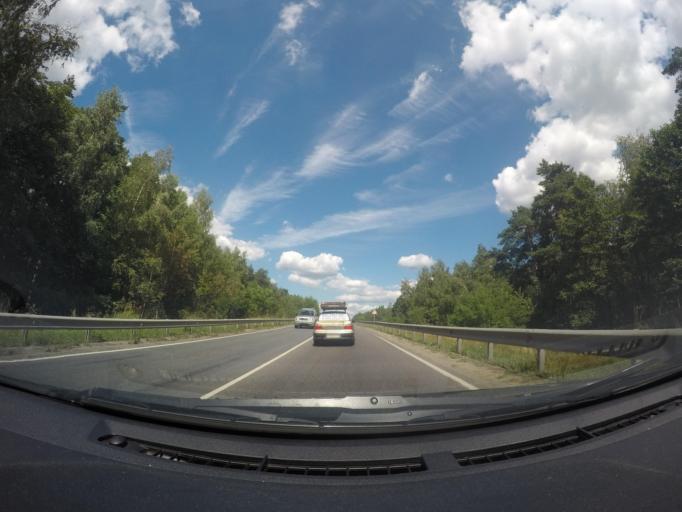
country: RU
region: Moskovskaya
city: Ramenskoye
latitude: 55.6318
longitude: 38.2859
